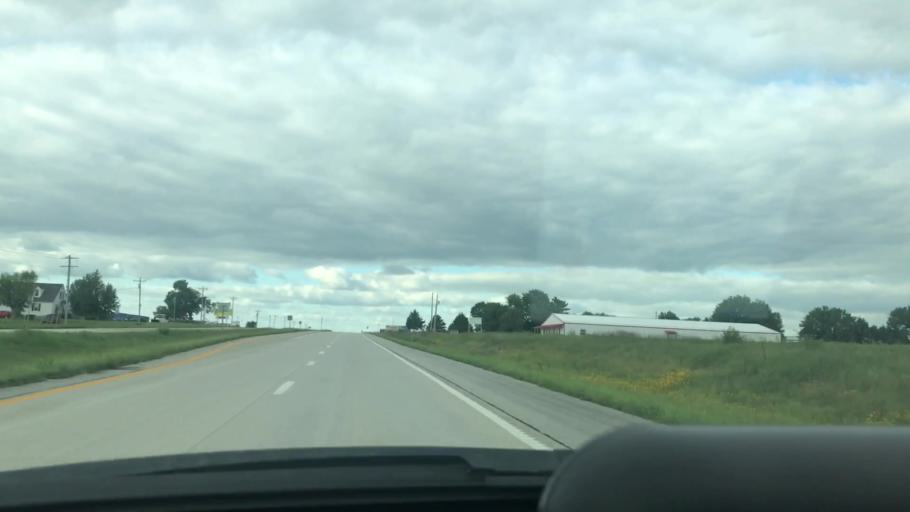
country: US
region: Missouri
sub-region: Benton County
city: Lincoln
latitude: 38.3382
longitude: -93.3406
